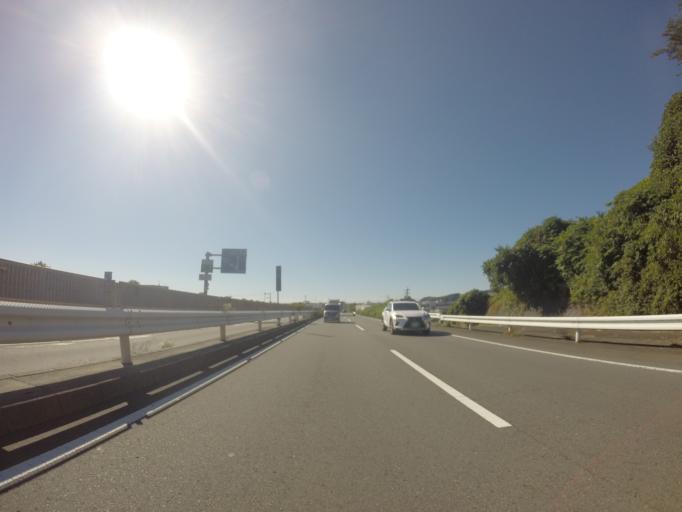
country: JP
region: Shizuoka
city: Fujieda
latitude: 34.9074
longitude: 138.2876
